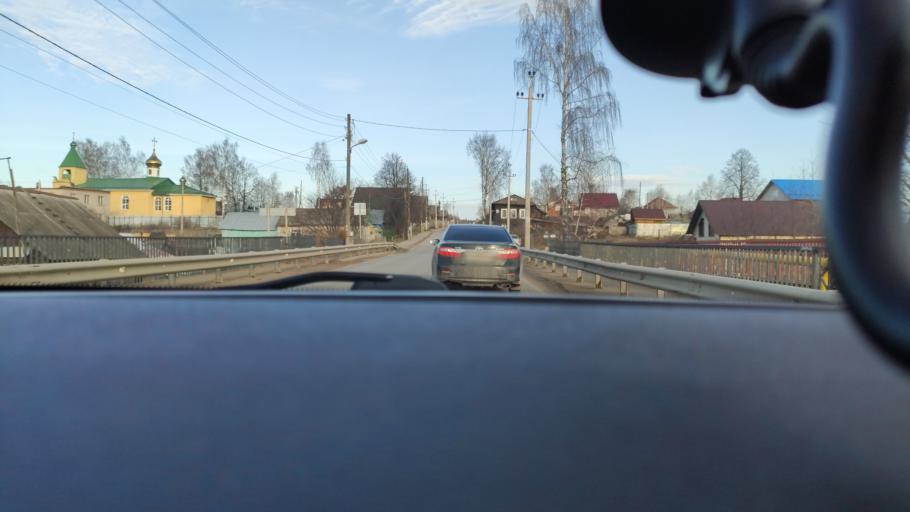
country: RU
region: Perm
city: Kondratovo
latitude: 58.0507
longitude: 56.0297
